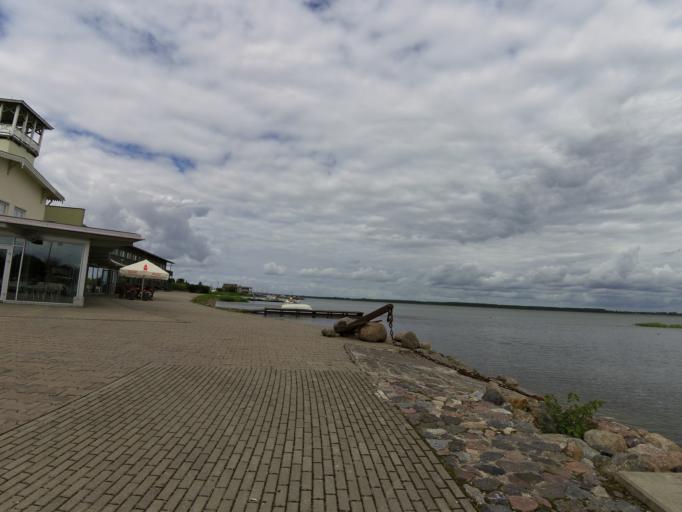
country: EE
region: Laeaene
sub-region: Haapsalu linn
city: Haapsalu
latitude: 58.9537
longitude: 23.5324
